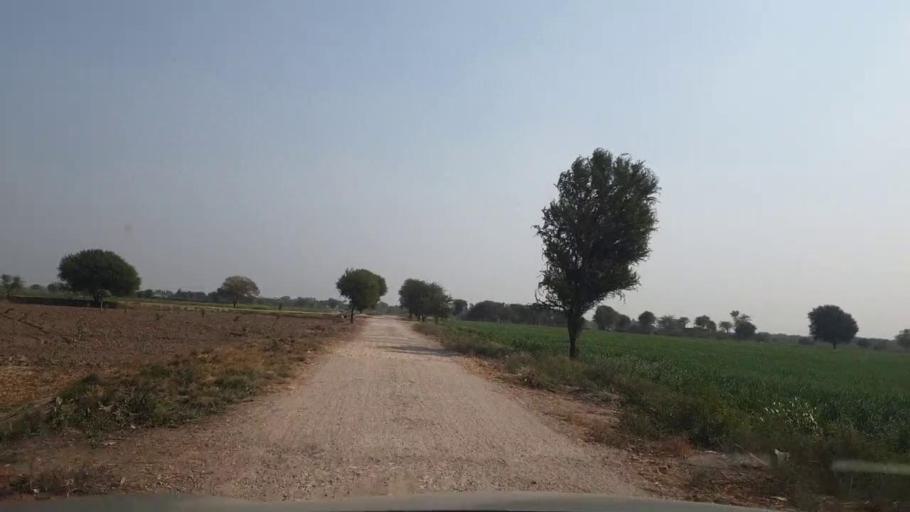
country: PK
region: Sindh
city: Tando Allahyar
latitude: 25.5626
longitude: 68.8243
